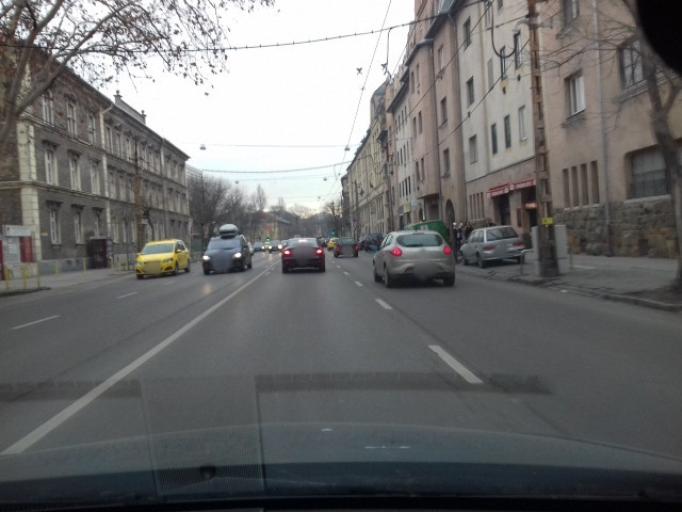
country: HU
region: Budapest
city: Budapest XIII. keruelet
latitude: 47.5218
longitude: 19.0675
